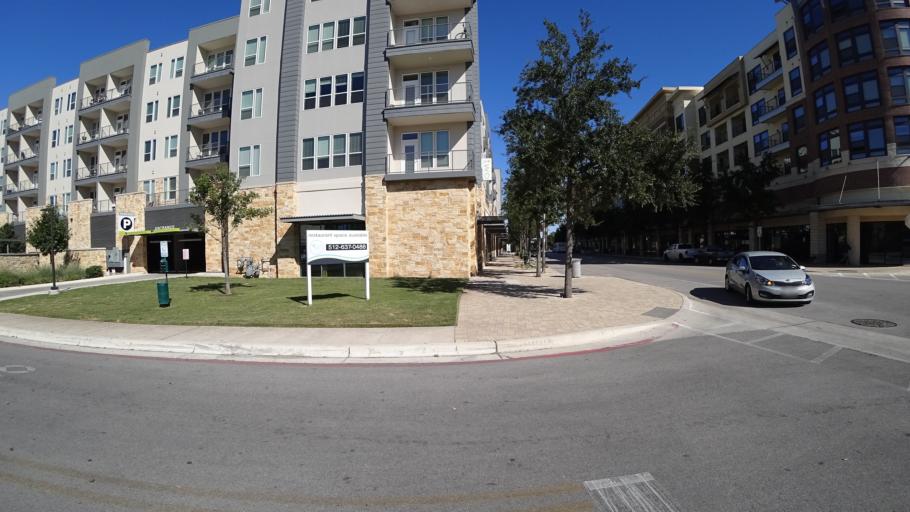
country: US
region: Texas
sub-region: Travis County
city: Austin
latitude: 30.2438
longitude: -97.7281
